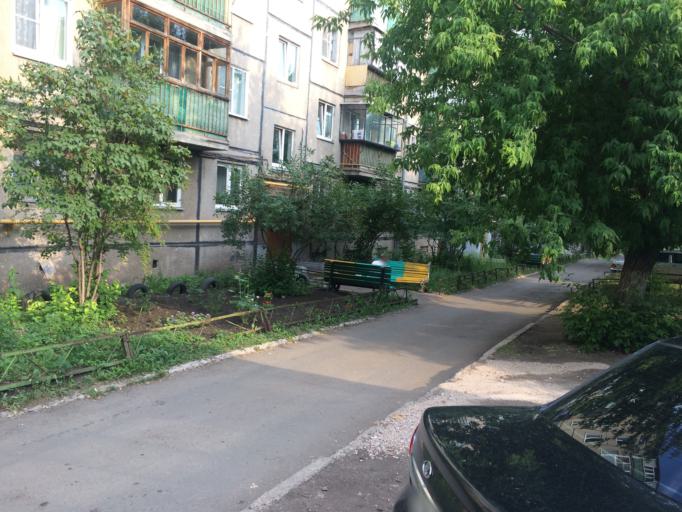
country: RU
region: Chelyabinsk
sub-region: Gorod Magnitogorsk
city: Magnitogorsk
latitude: 53.4067
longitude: 58.9774
